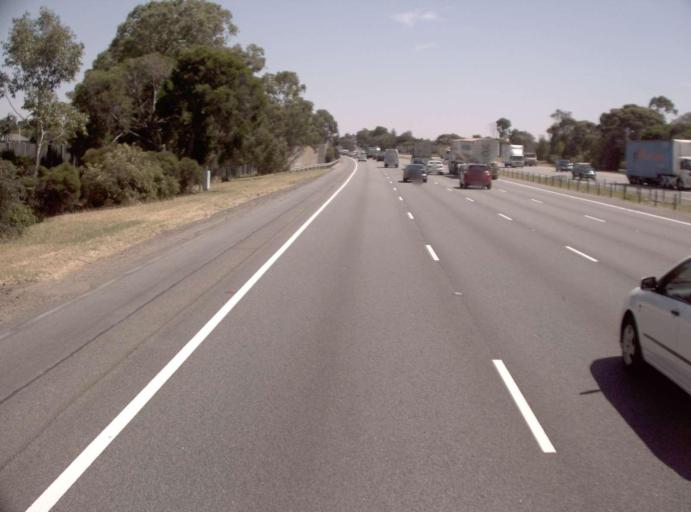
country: AU
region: Victoria
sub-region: Monash
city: Notting Hill
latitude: -37.9147
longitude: 145.1677
